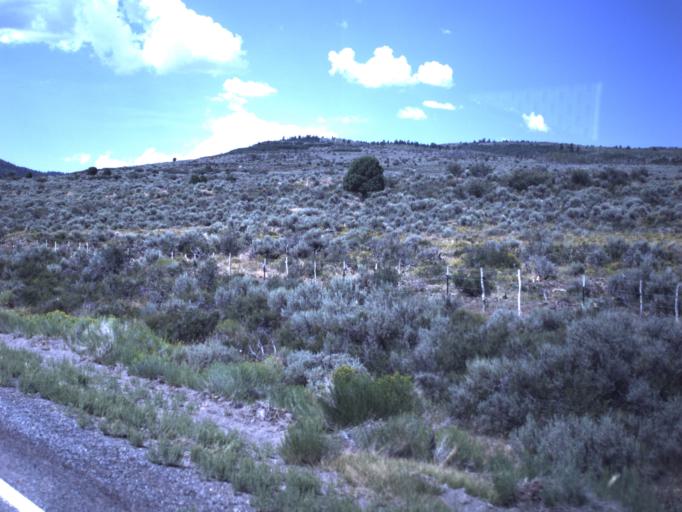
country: US
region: Utah
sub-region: Carbon County
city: Helper
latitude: 39.8596
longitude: -111.0475
